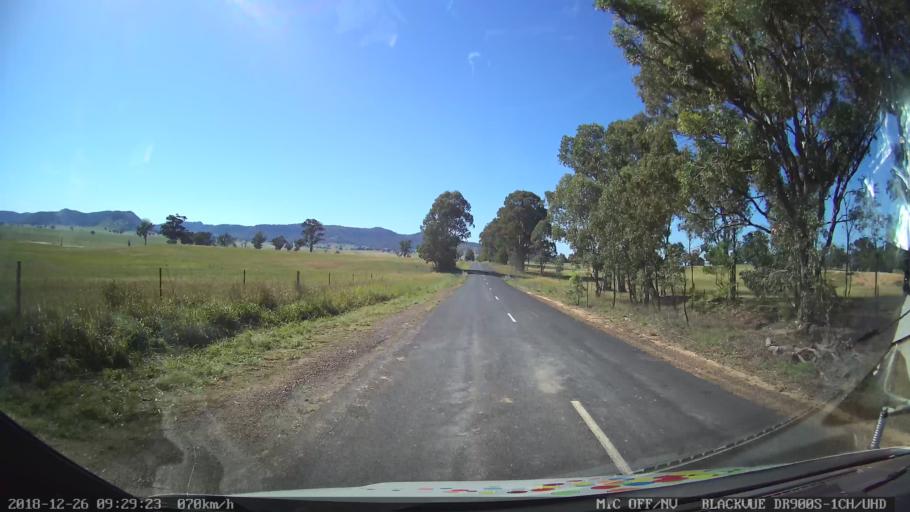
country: AU
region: New South Wales
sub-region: Mid-Western Regional
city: Kandos
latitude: -32.8524
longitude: 150.0272
